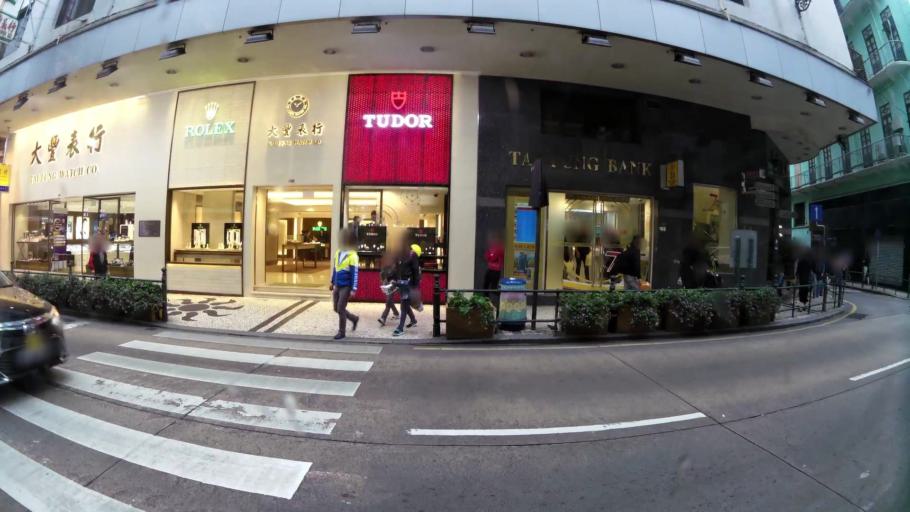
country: MO
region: Macau
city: Macau
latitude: 22.1942
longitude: 113.5390
